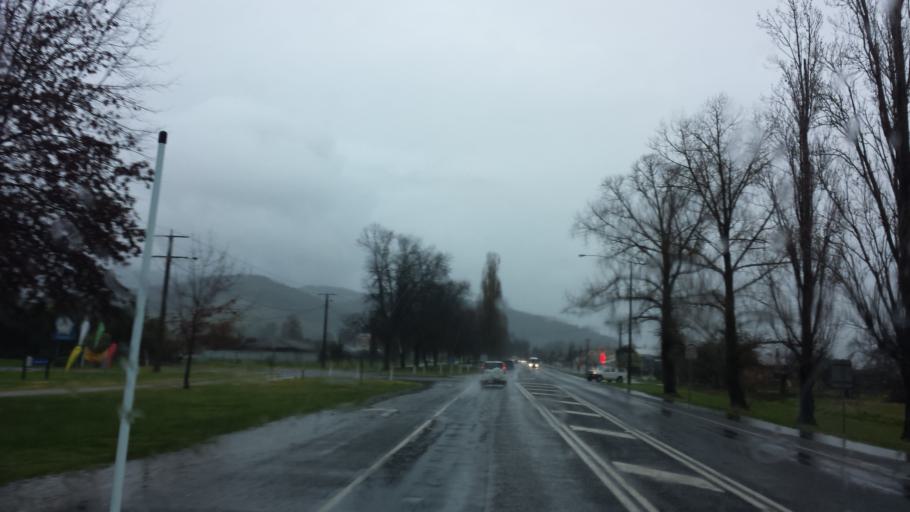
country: AU
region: Victoria
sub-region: Wangaratta
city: Wangaratta
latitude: -36.5548
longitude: 146.7140
